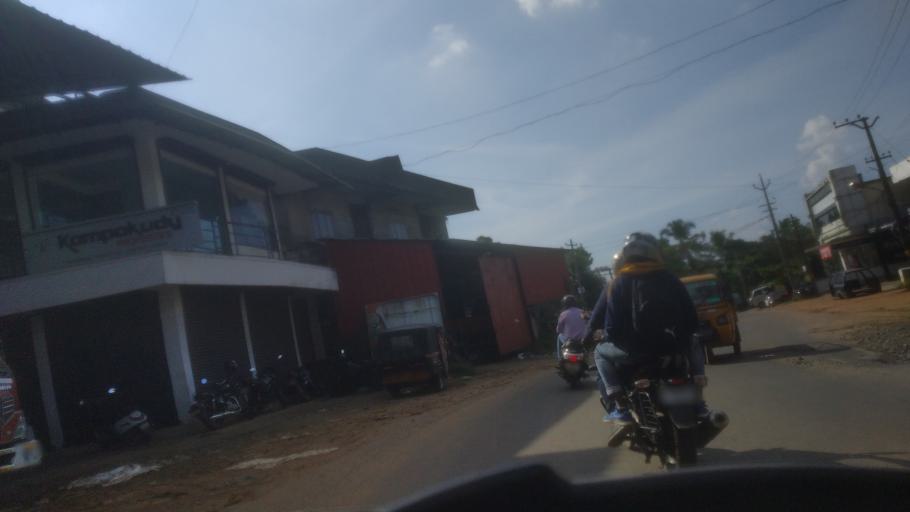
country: IN
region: Kerala
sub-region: Ernakulam
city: Muvattupula
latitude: 9.9930
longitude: 76.5833
